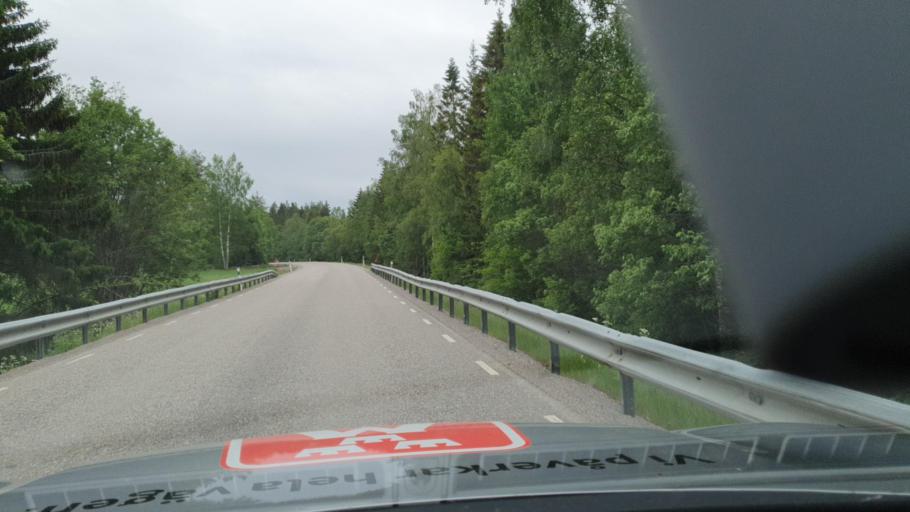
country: SE
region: Vaesternorrland
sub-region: Kramfors Kommun
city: Kramfors
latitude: 62.9534
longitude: 17.9024
